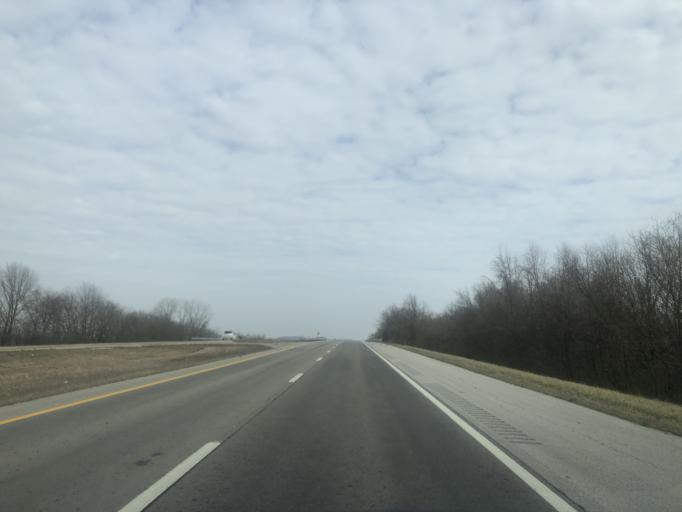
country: US
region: Tennessee
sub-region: Maury County
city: Mount Pleasant
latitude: 35.5786
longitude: -87.1469
